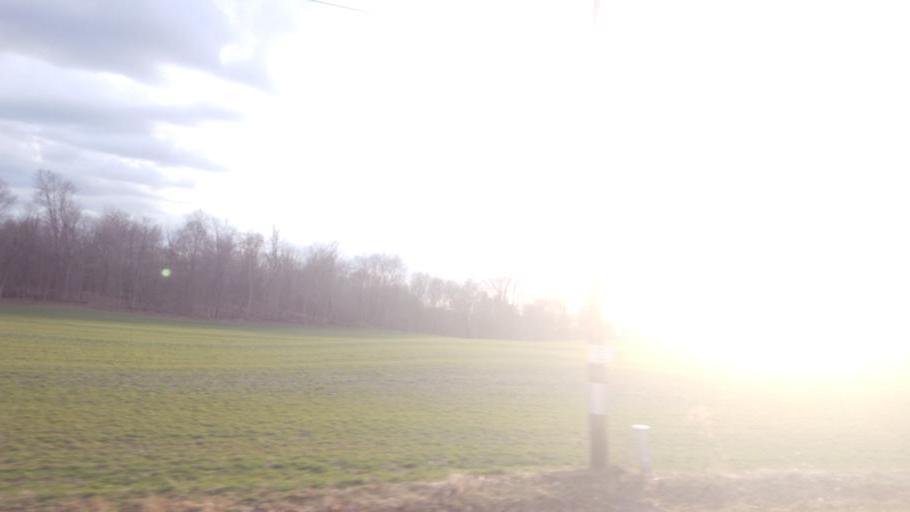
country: US
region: Ohio
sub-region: Knox County
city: Fredericktown
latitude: 40.4691
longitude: -82.6516
